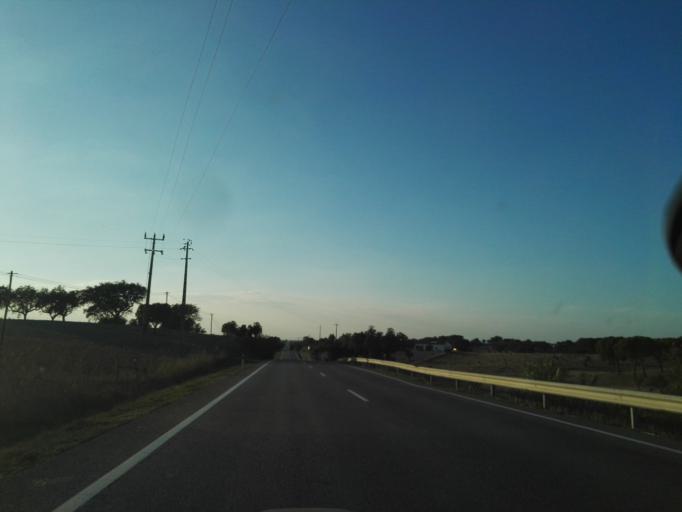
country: PT
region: Evora
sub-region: Arraiolos
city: Arraiolos
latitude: 38.8341
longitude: -7.8488
